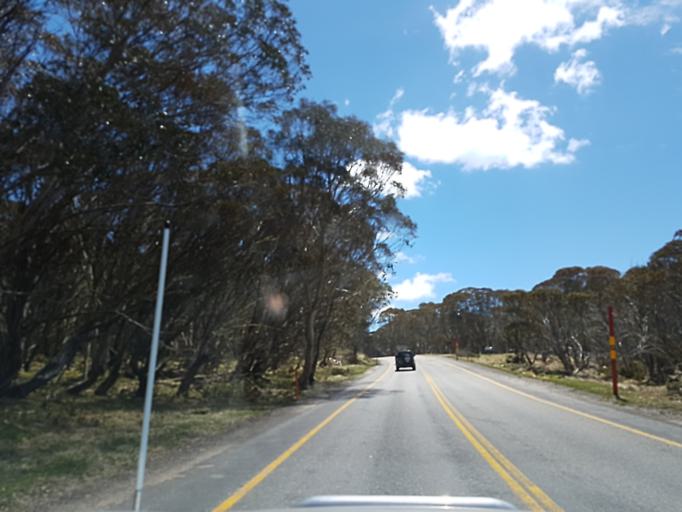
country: AU
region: Victoria
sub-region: Alpine
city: Mount Beauty
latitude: -37.0118
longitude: 147.1897
